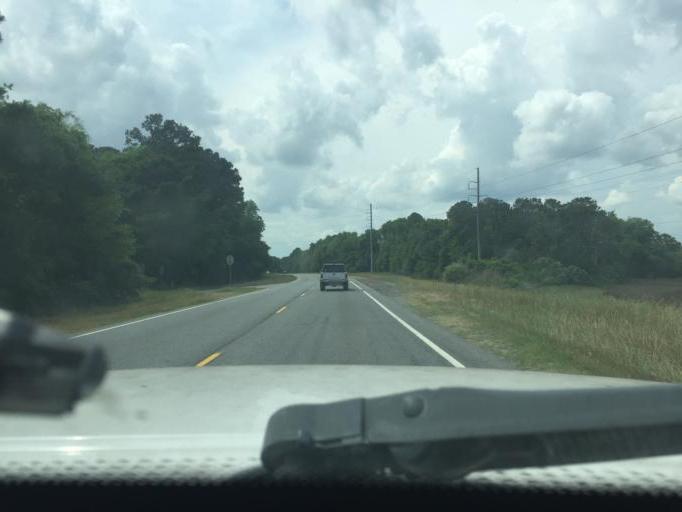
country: US
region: Georgia
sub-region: Chatham County
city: Montgomery
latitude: 31.9540
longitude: -81.0890
